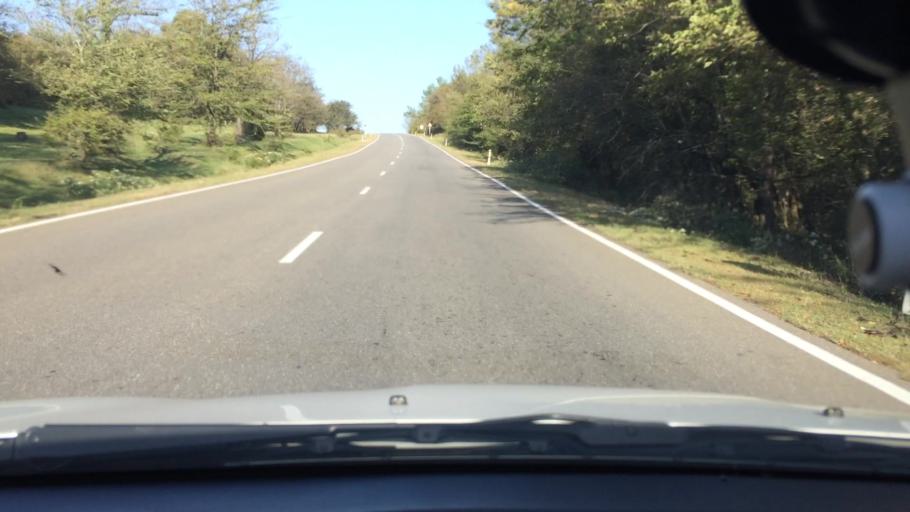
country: GE
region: Imereti
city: Kutaisi
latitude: 42.2503
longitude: 42.7539
